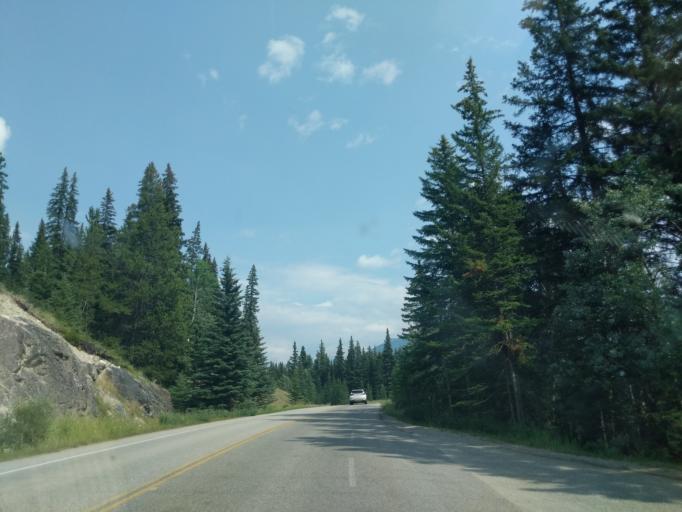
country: CA
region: Alberta
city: Banff
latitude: 51.1686
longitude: -115.6863
